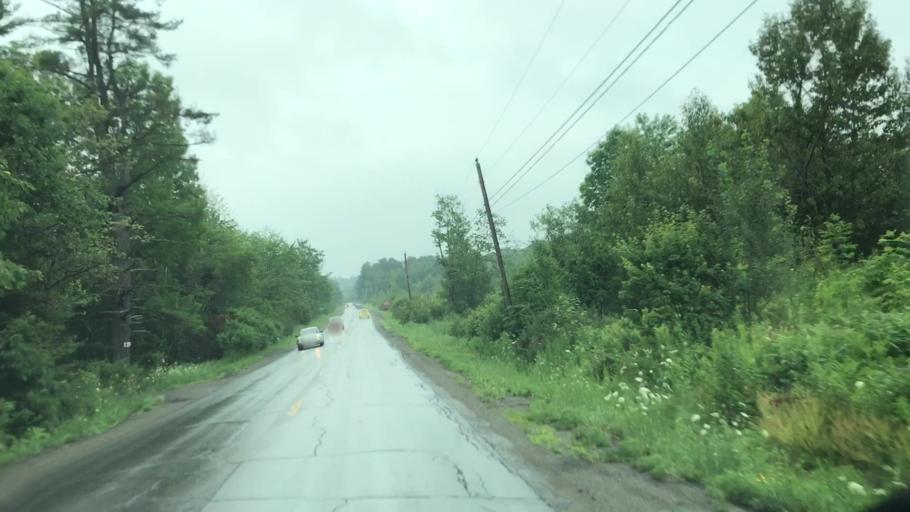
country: US
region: Maine
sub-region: Penobscot County
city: Veazie
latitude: 44.8623
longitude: -68.7224
